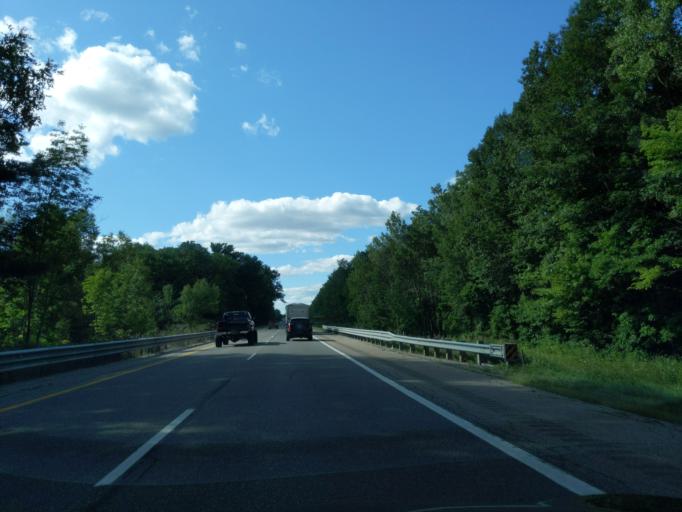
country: US
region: Michigan
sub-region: Muskegon County
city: Fruitport
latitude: 43.1147
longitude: -86.1253
